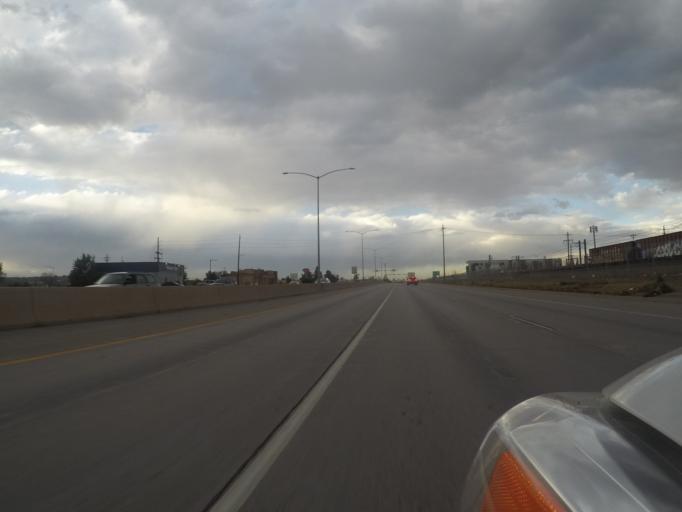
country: US
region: Colorado
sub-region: Arapahoe County
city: Sheridan
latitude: 39.6376
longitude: -105.0071
